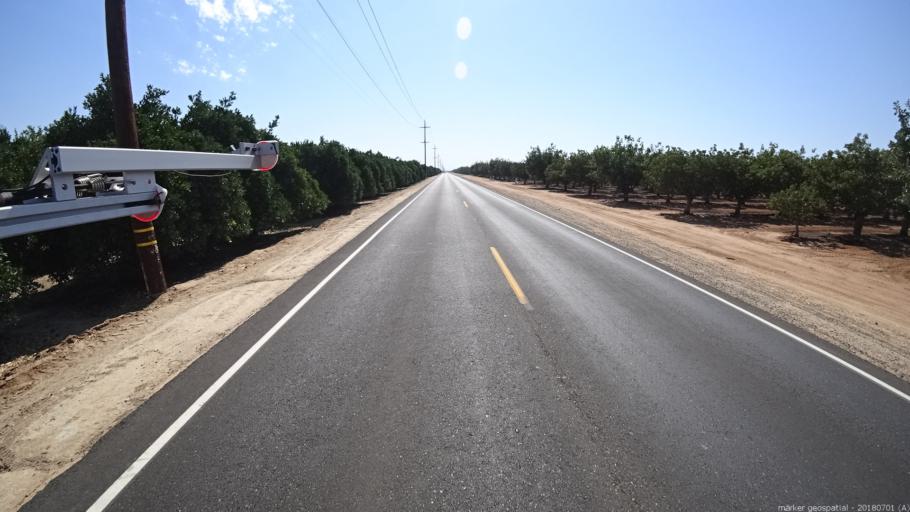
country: US
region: California
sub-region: Madera County
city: Bonadelle Ranchos-Madera Ranchos
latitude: 36.8804
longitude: -119.8653
